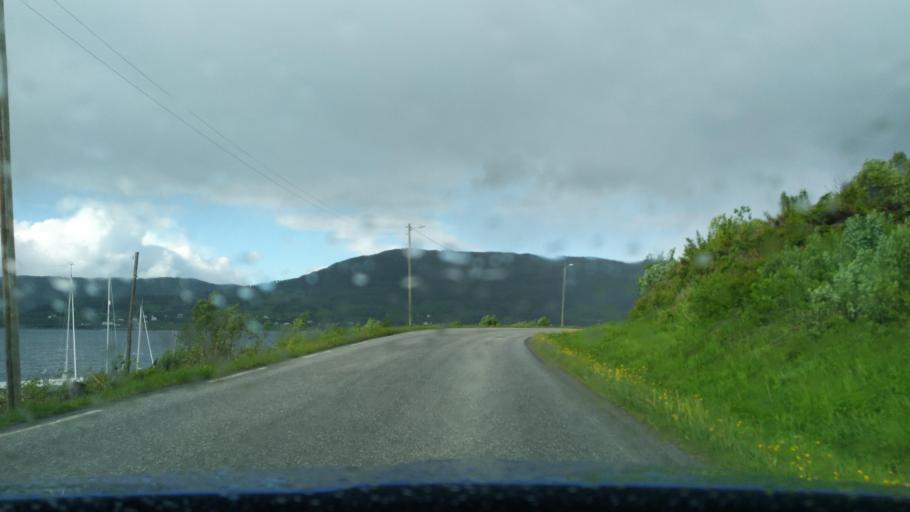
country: NO
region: Troms
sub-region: Sorreisa
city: Sorreisa
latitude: 69.1410
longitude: 18.1200
